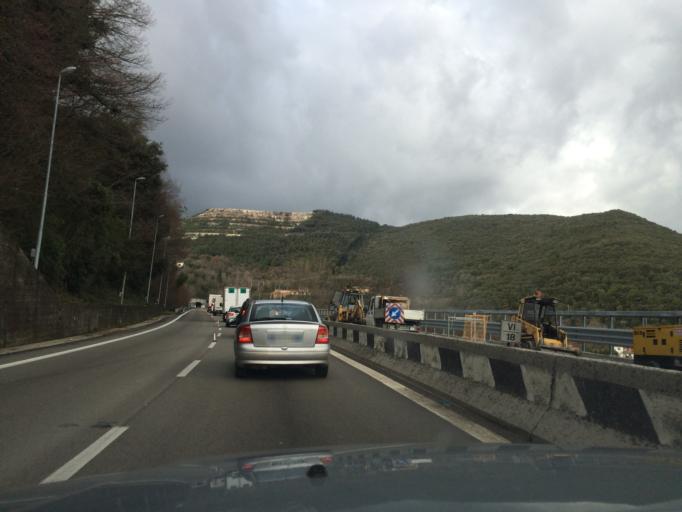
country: IT
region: Umbria
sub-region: Provincia di Terni
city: Narni Scalo
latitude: 42.5419
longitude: 12.4979
